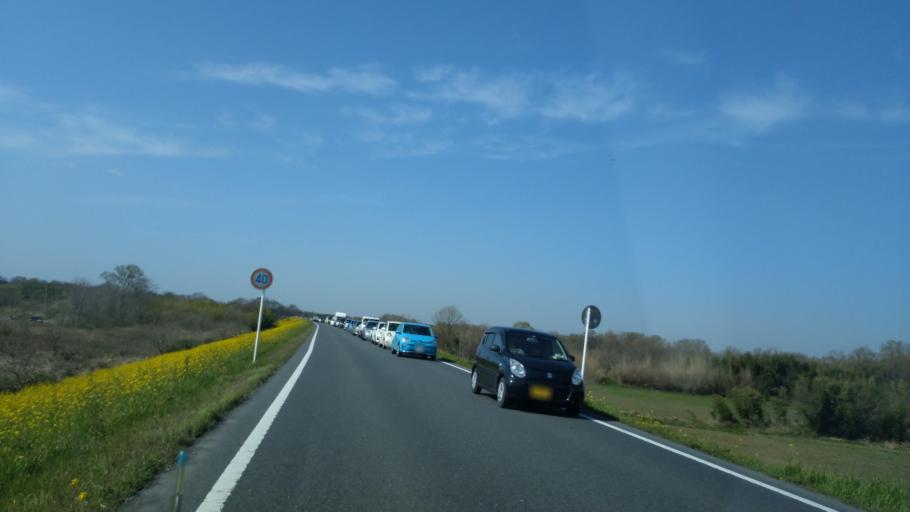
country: JP
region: Saitama
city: Okegawa
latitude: 35.9452
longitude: 139.5355
